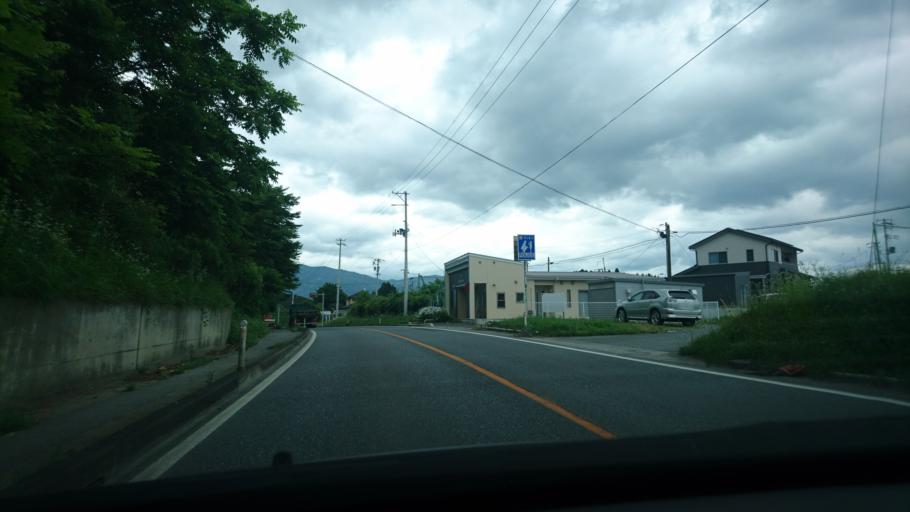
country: JP
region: Iwate
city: Ofunato
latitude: 38.9935
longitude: 141.6176
